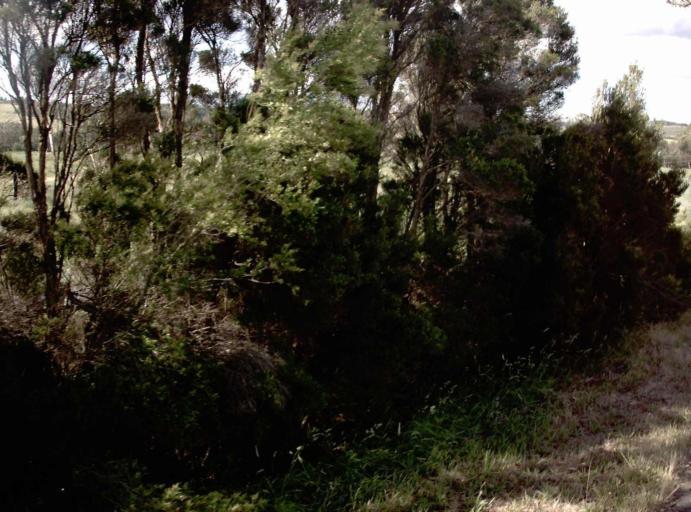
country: AU
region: Victoria
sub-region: Latrobe
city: Morwell
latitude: -38.1706
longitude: 146.4085
